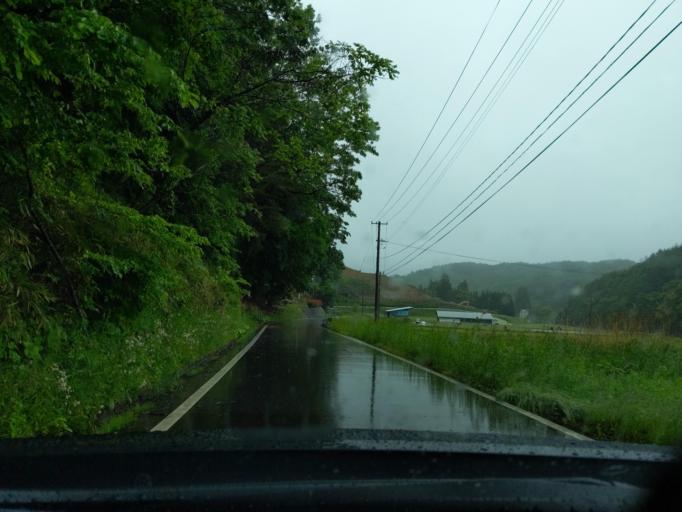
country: JP
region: Fukushima
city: Yanagawamachi-saiwaicho
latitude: 37.6432
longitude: 140.7305
